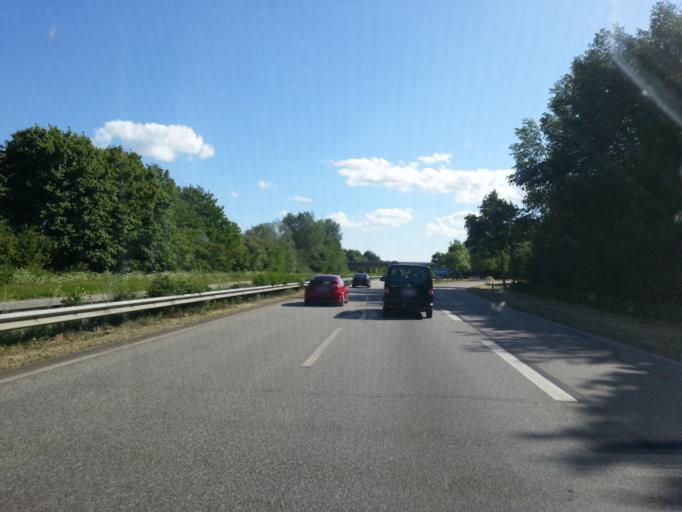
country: DE
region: Schleswig-Holstein
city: Sierksdorf
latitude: 54.0970
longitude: 10.7777
